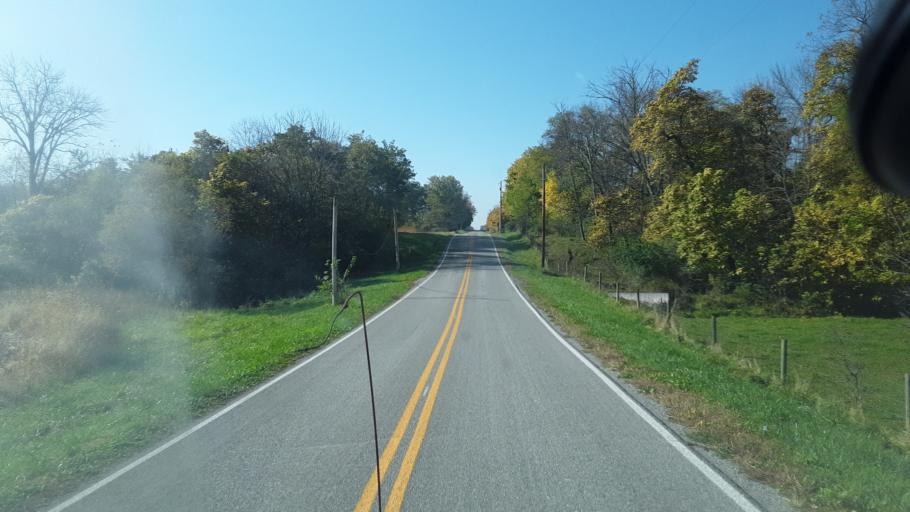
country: US
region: Ohio
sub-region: Highland County
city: Leesburg
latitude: 39.2677
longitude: -83.5446
